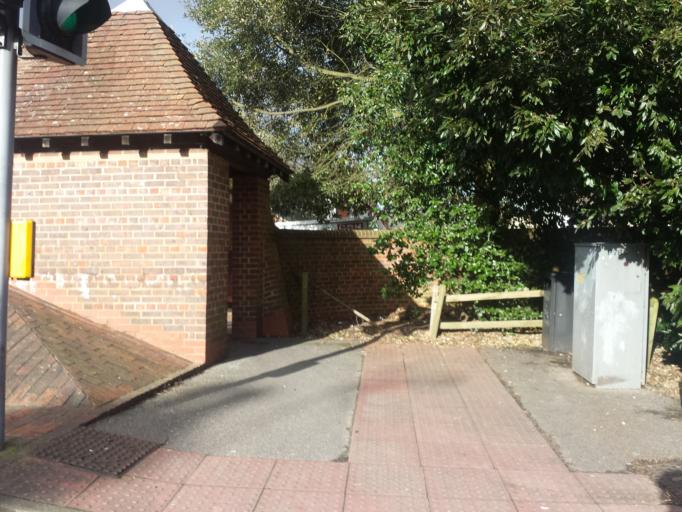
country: GB
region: England
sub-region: Surrey
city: Godalming
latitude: 51.1846
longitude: -0.6111
